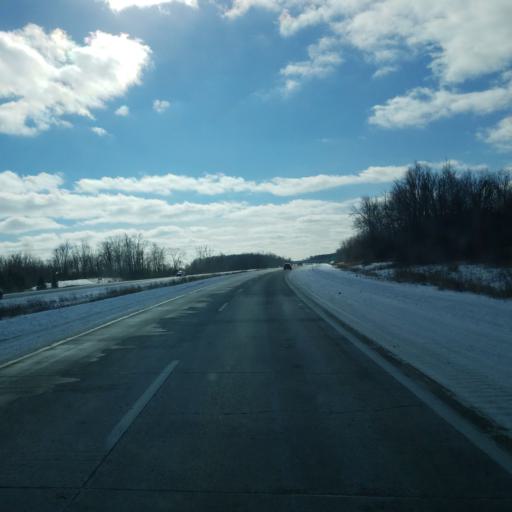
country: US
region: Michigan
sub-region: Clinton County
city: DeWitt
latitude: 42.8805
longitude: -84.5153
